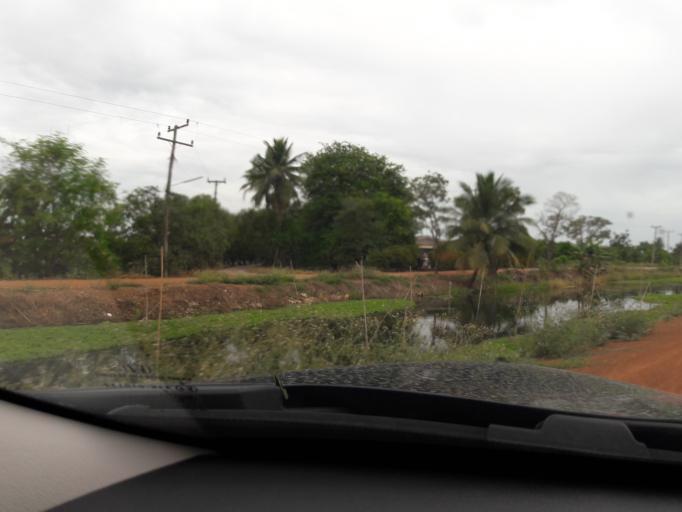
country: TH
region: Ratchaburi
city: Bang Phae
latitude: 13.6160
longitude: 99.9653
